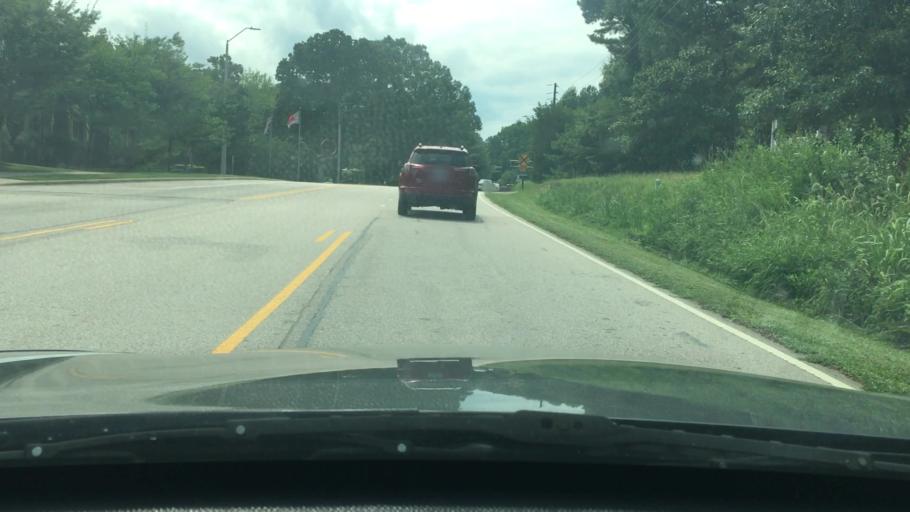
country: US
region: North Carolina
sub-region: Wake County
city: Cary
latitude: 35.7863
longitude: -78.7931
